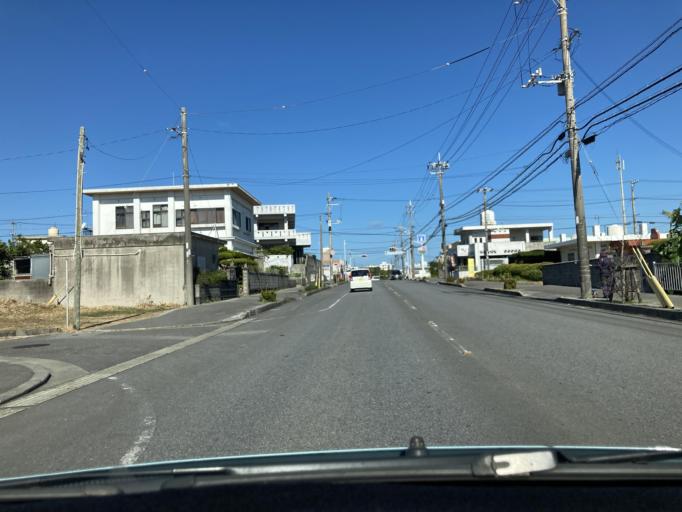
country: JP
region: Okinawa
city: Gushikawa
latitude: 26.3754
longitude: 127.8643
